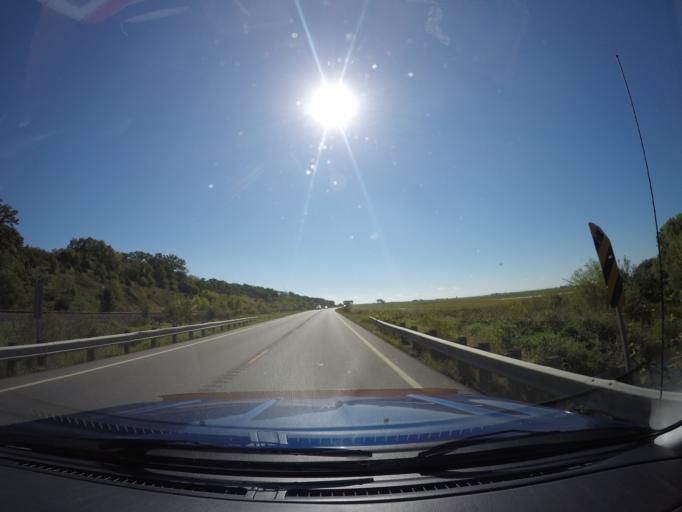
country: US
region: Kansas
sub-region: Pottawatomie County
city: Saint Marys
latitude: 39.1802
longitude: -96.0358
